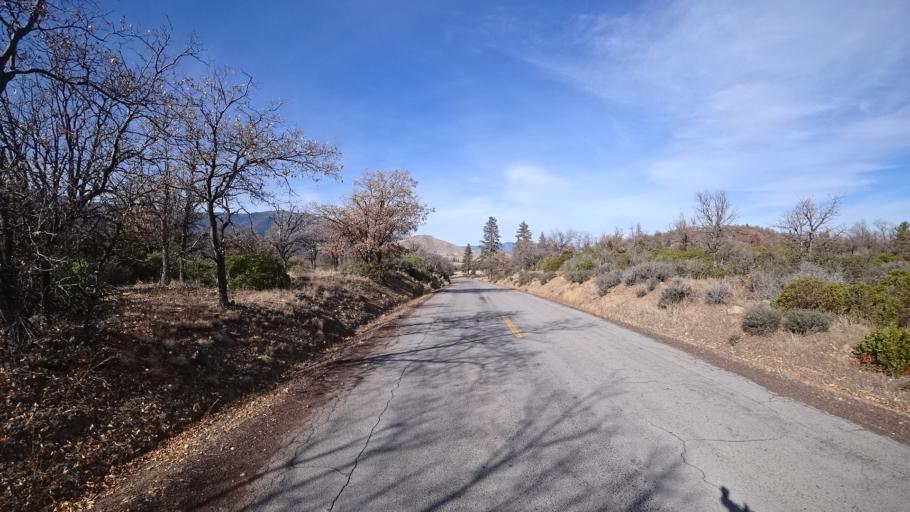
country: US
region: California
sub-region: Siskiyou County
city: Weed
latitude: 41.4315
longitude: -122.4260
